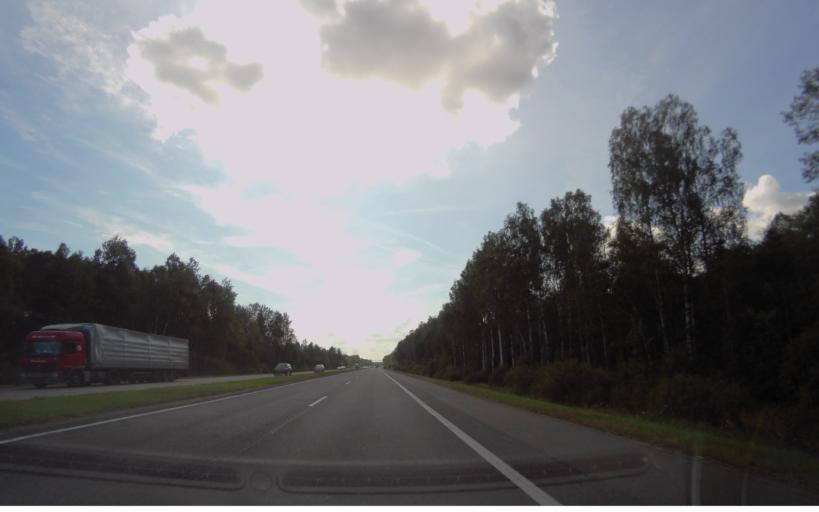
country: BY
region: Minsk
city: Horad Barysaw
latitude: 54.0900
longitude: 28.4878
